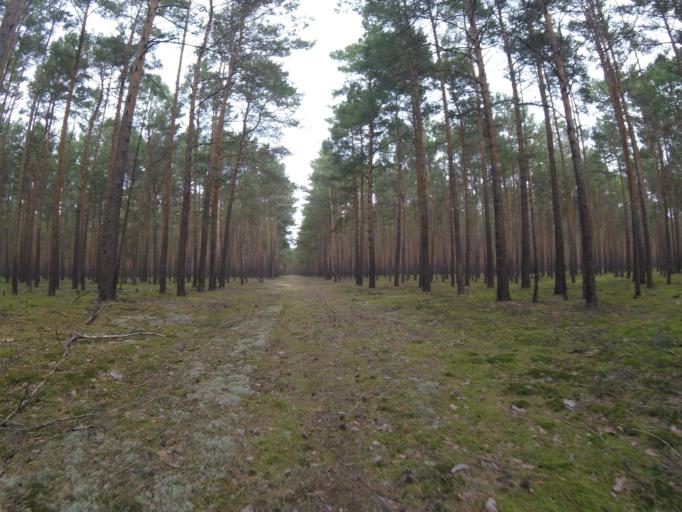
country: DE
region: Brandenburg
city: Gross Koris
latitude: 52.1892
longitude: 13.6828
